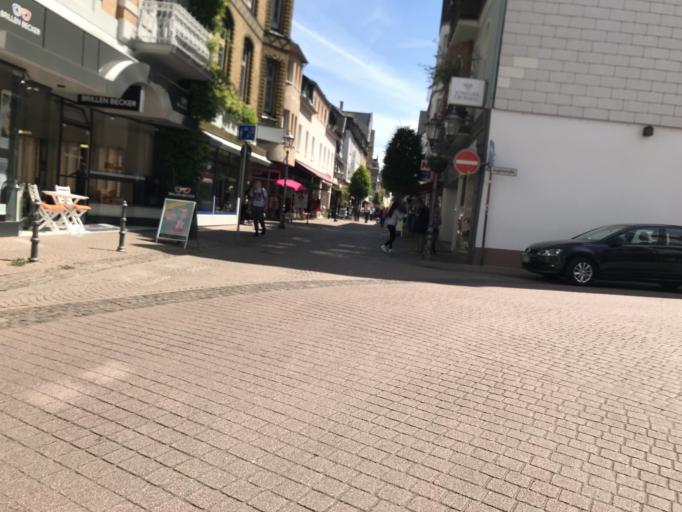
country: DE
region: Rheinland-Pfalz
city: Boppard
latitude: 50.2317
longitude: 7.5893
